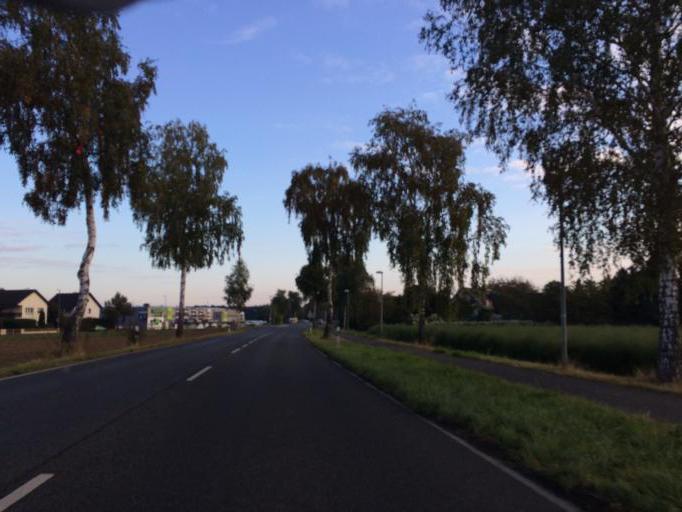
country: DE
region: North Rhine-Westphalia
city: Sankt Augustin
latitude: 50.7644
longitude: 7.1752
